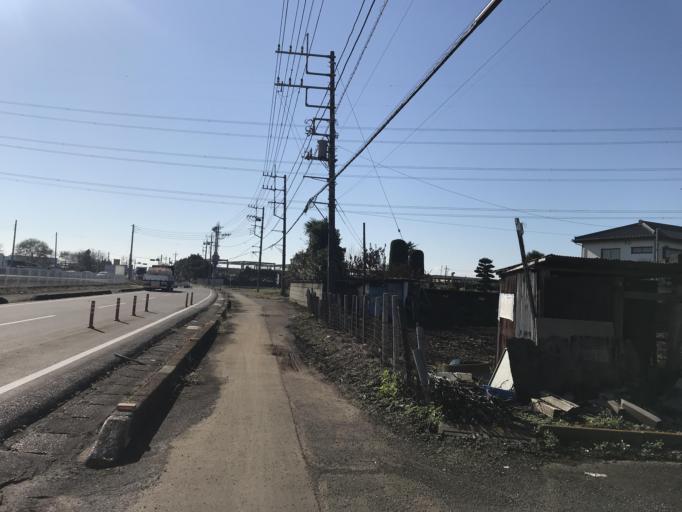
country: JP
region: Ibaraki
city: Sakai
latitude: 36.1352
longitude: 139.8063
